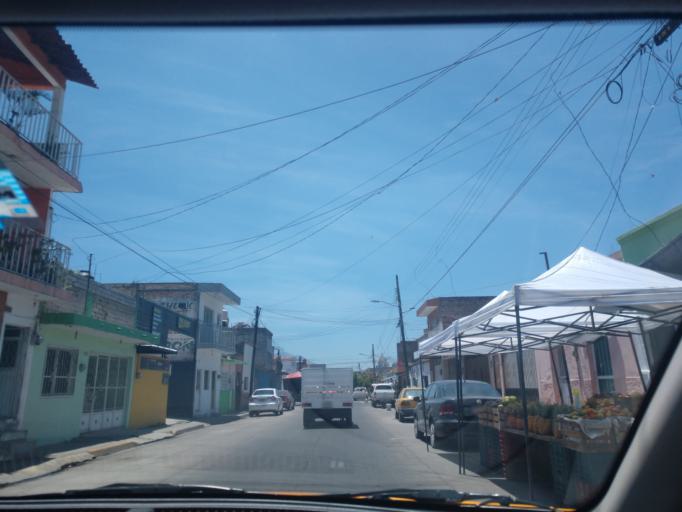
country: MX
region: Nayarit
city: Tepic
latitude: 21.5179
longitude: -104.9015
